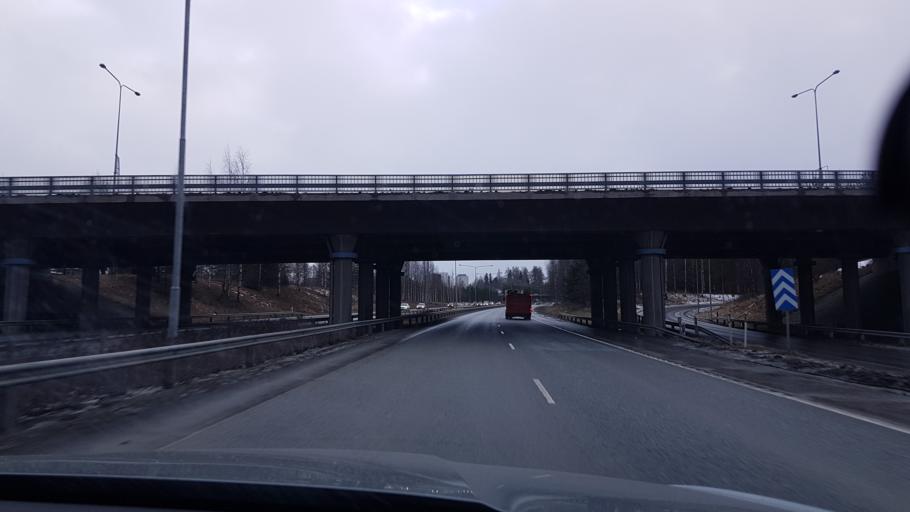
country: FI
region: Pirkanmaa
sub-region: Tampere
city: Tampere
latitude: 61.4785
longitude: 23.8712
